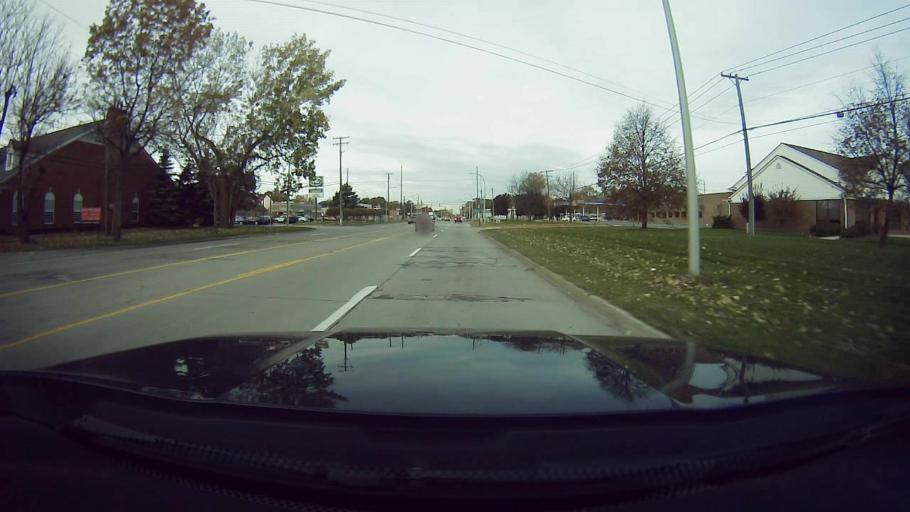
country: US
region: Michigan
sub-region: Oakland County
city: Madison Heights
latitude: 42.4910
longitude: -83.0790
